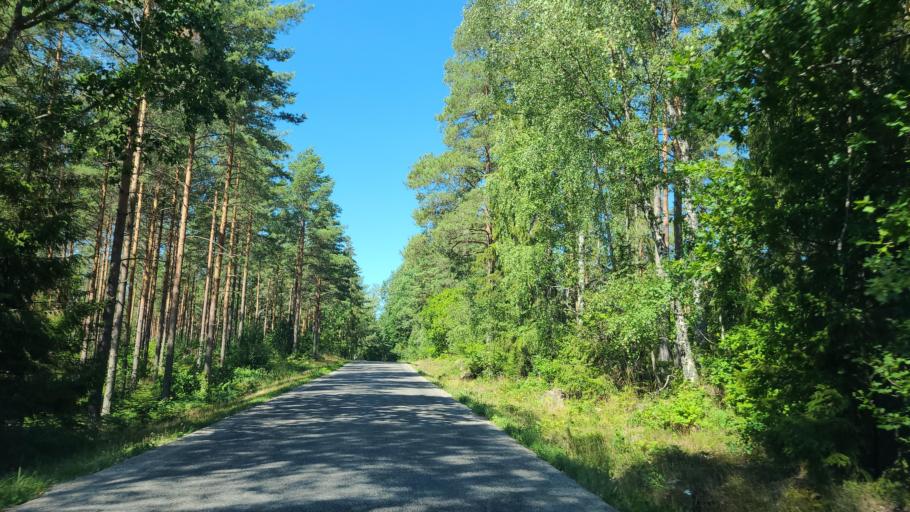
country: SE
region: Kalmar
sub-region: Kalmar Kommun
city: Ljungbyholm
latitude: 56.5703
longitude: 16.0470
